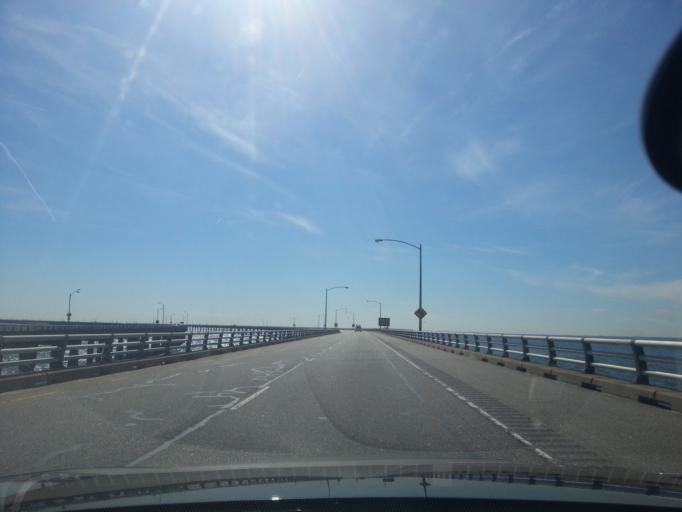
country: US
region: Virginia
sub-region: City of Virginia Beach
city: Virginia Beach
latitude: 37.0335
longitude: -76.0814
